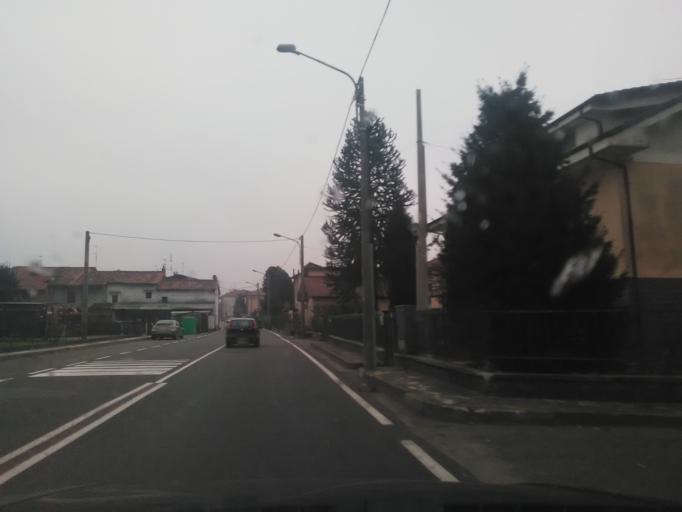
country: IT
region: Piedmont
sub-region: Provincia di Biella
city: Cavaglia
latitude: 45.4084
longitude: 8.0919
